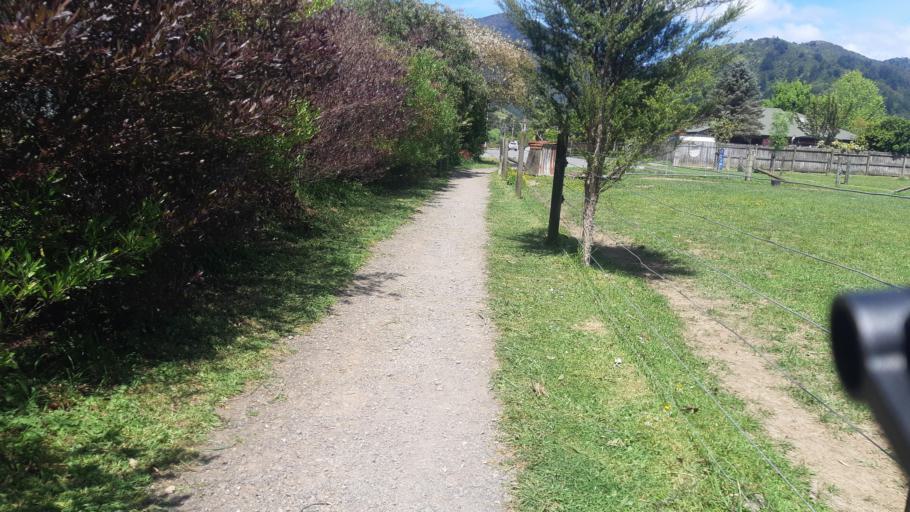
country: NZ
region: Marlborough
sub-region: Marlborough District
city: Picton
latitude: -41.2713
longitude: 174.0297
